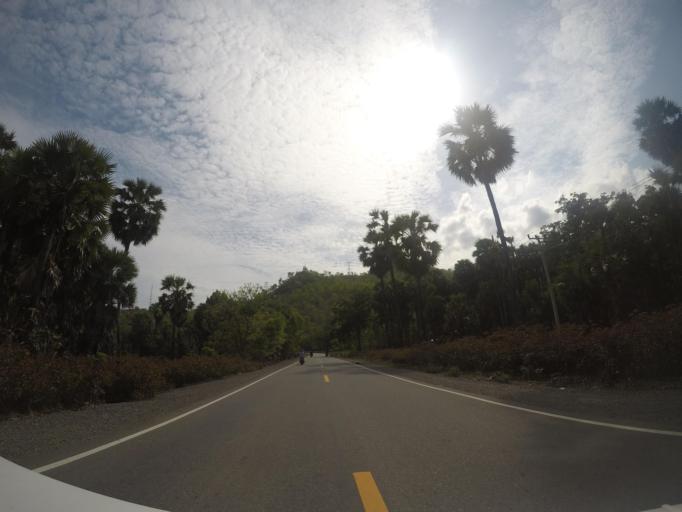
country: ID
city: Metinaro
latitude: -8.4836
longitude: 125.8414
